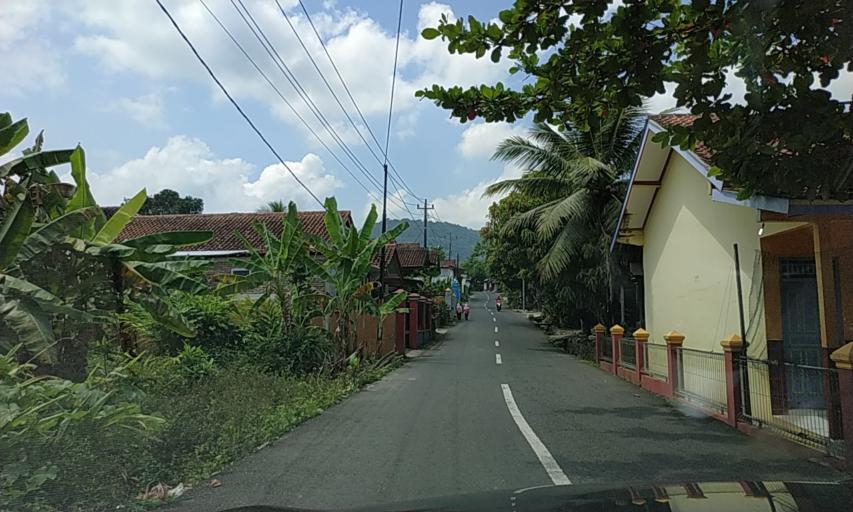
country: ID
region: Central Java
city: Kutoarjo
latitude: -7.6249
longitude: 109.7244
